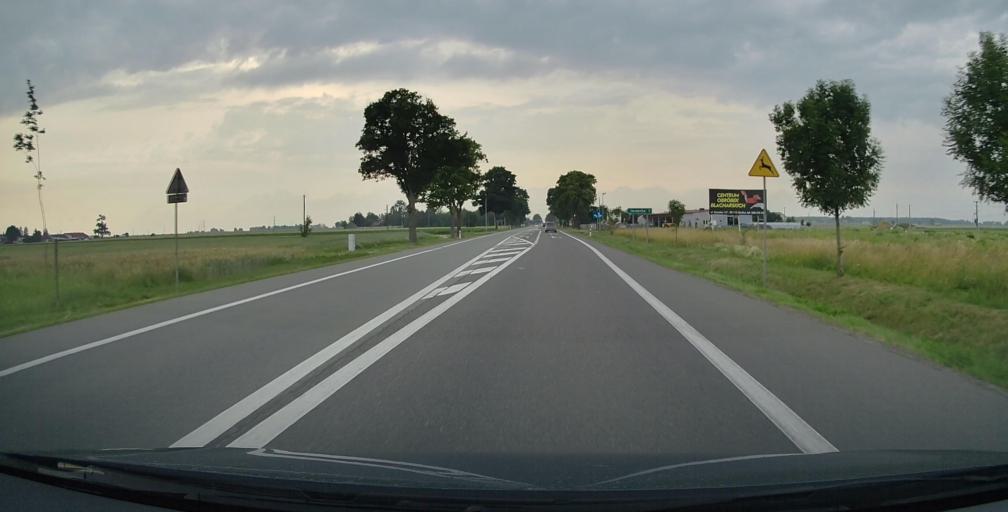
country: PL
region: Masovian Voivodeship
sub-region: Powiat siedlecki
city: Zbuczyn
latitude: 52.1052
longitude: 22.3936
